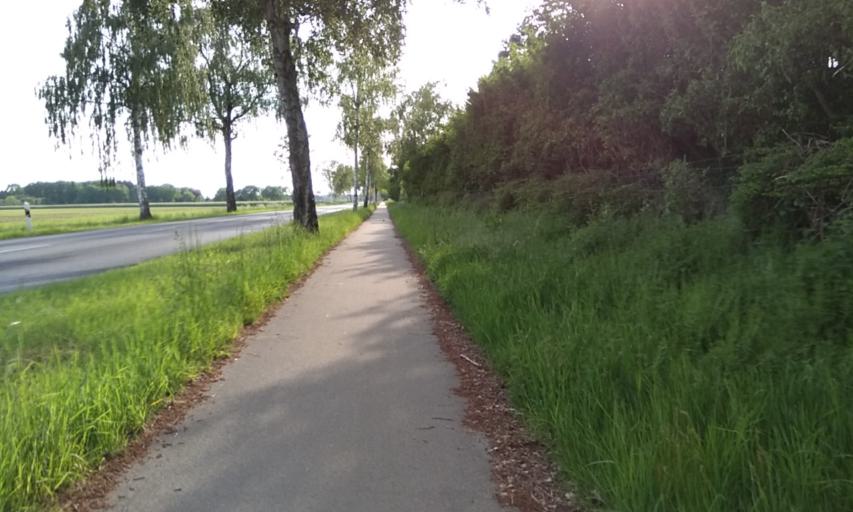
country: DE
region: Lower Saxony
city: Apensen
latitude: 53.4321
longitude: 9.6068
